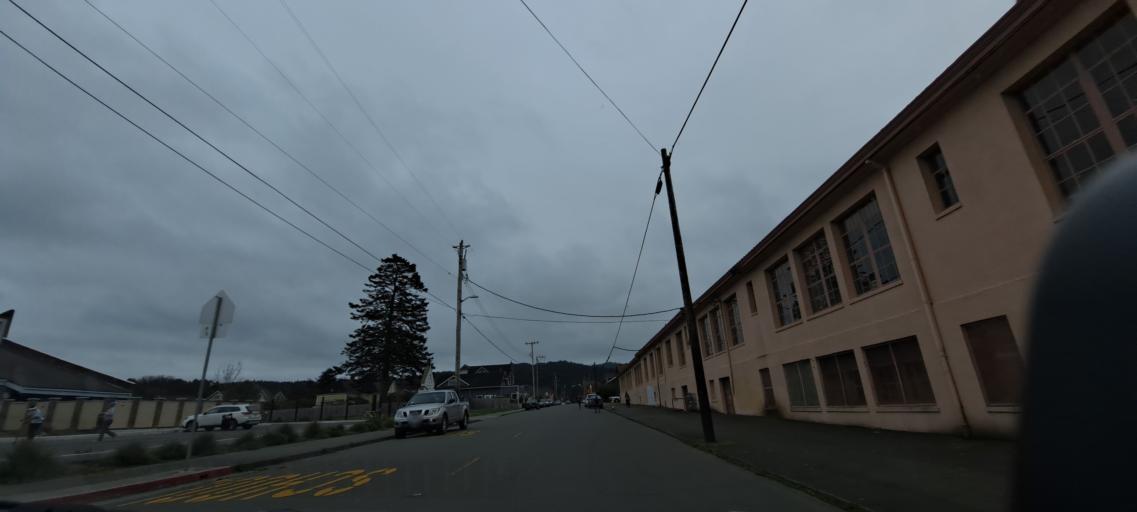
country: US
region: California
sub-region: Humboldt County
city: Arcata
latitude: 40.8754
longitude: -124.0884
